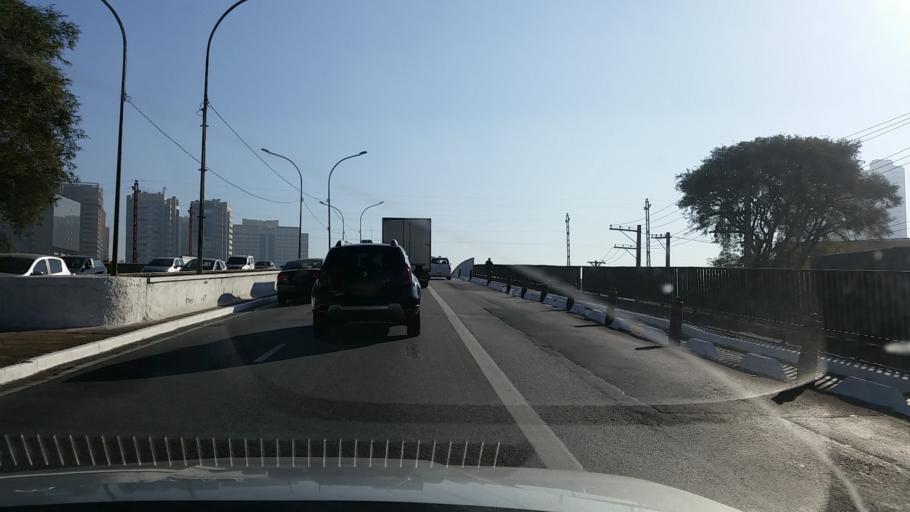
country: BR
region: Sao Paulo
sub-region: Sao Paulo
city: Sao Paulo
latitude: -23.5272
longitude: -46.6605
